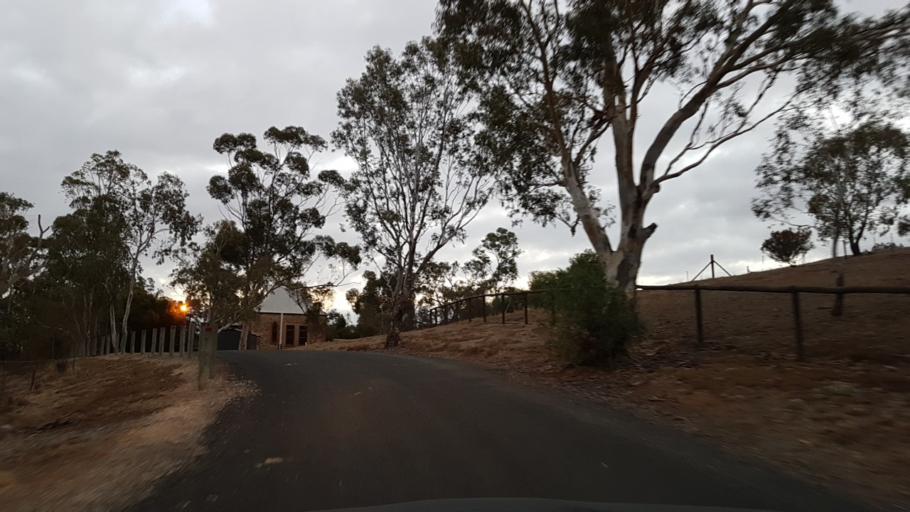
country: AU
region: South Australia
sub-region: Mount Barker
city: Callington
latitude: -35.0698
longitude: 139.0141
